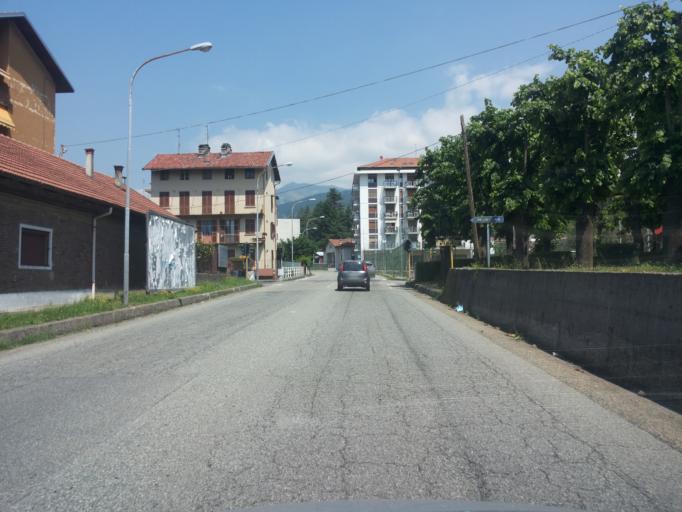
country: IT
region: Piedmont
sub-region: Provincia di Biella
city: Andorno Cacciorna
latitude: 45.6118
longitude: 8.0523
